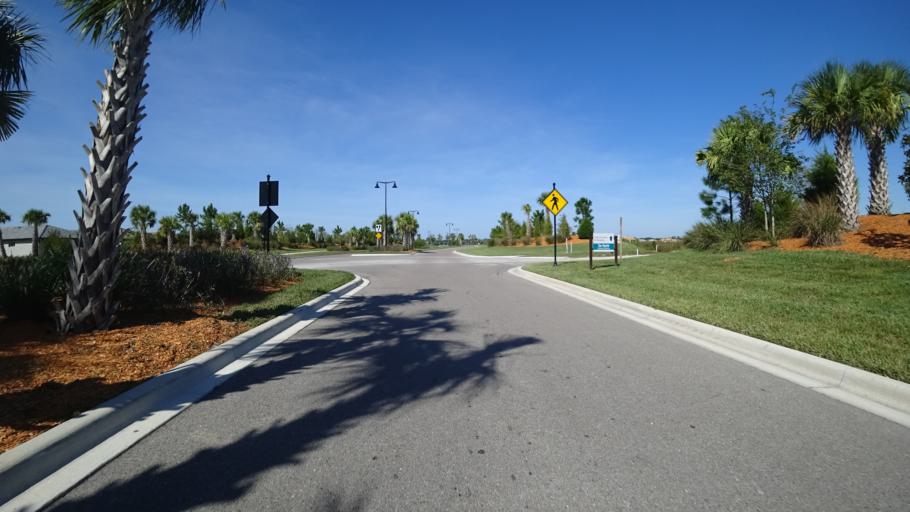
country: US
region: Florida
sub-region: Sarasota County
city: The Meadows
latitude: 27.4086
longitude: -82.3614
